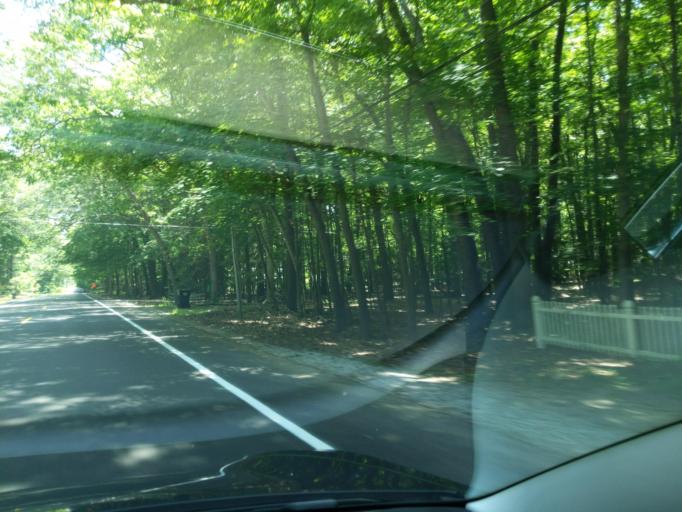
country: US
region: Michigan
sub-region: Muskegon County
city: Montague
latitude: 43.3832
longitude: -86.4183
